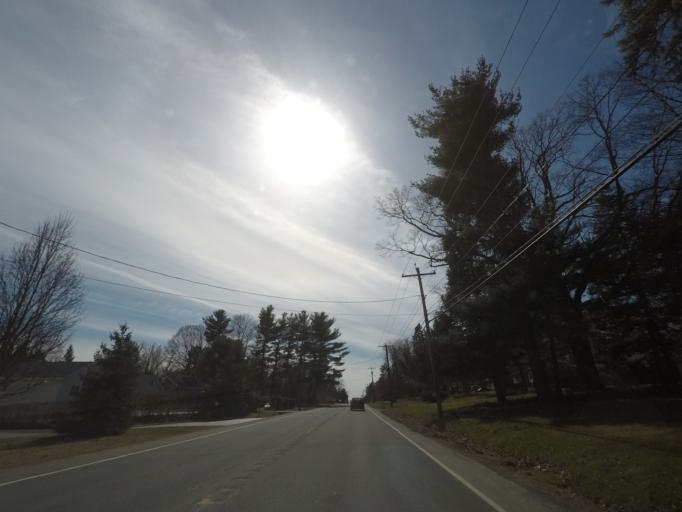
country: US
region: New York
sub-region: Albany County
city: Cohoes
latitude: 42.7701
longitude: -73.7334
